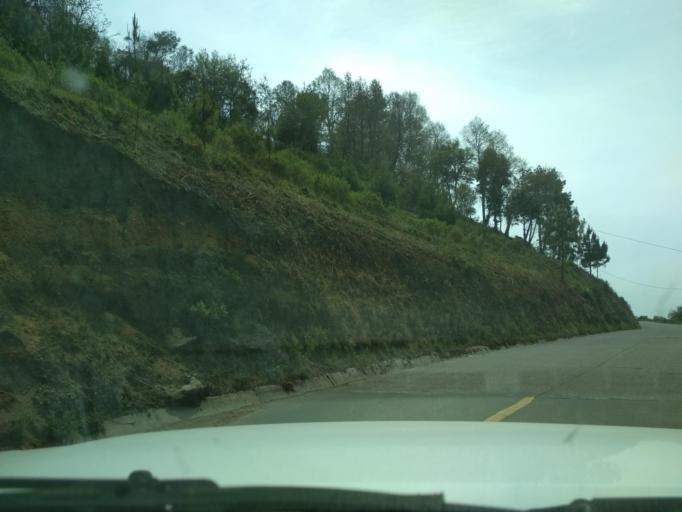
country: MX
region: Veracruz
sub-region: Mariano Escobedo
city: San Isidro el Berro
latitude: 18.9759
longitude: -97.2109
